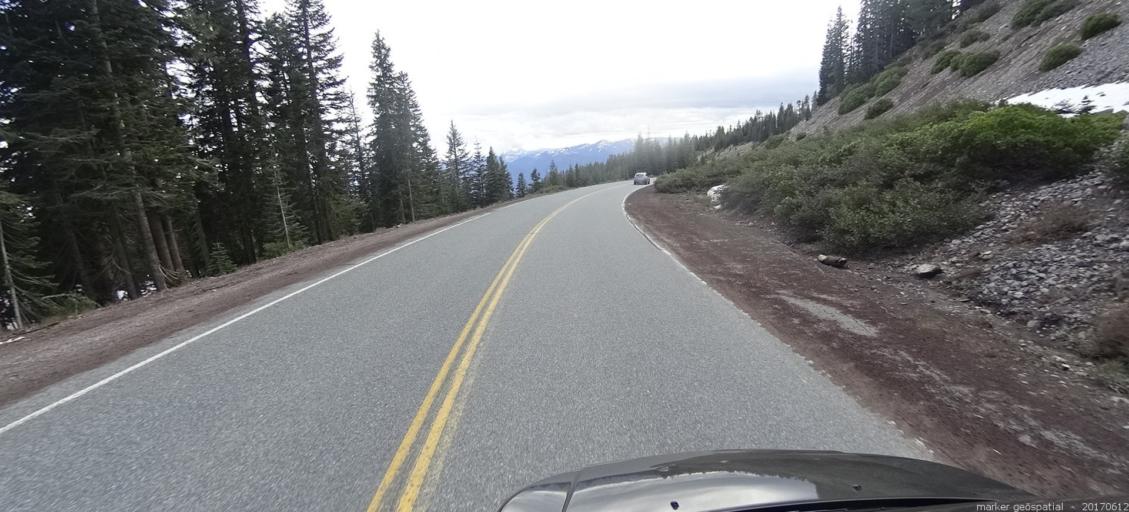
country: US
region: California
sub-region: Siskiyou County
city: Mount Shasta
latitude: 41.3524
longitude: -122.2348
